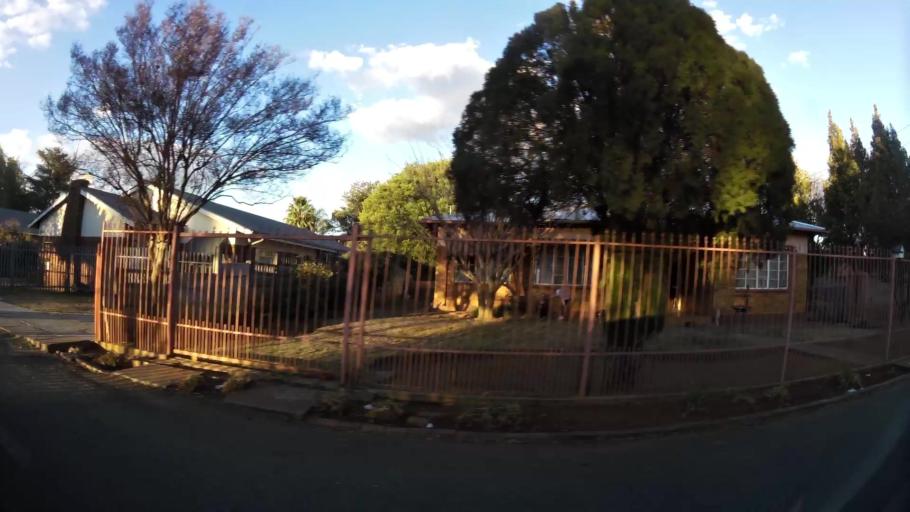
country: ZA
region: North-West
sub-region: Dr Kenneth Kaunda District Municipality
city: Potchefstroom
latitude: -26.7188
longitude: 27.0916
